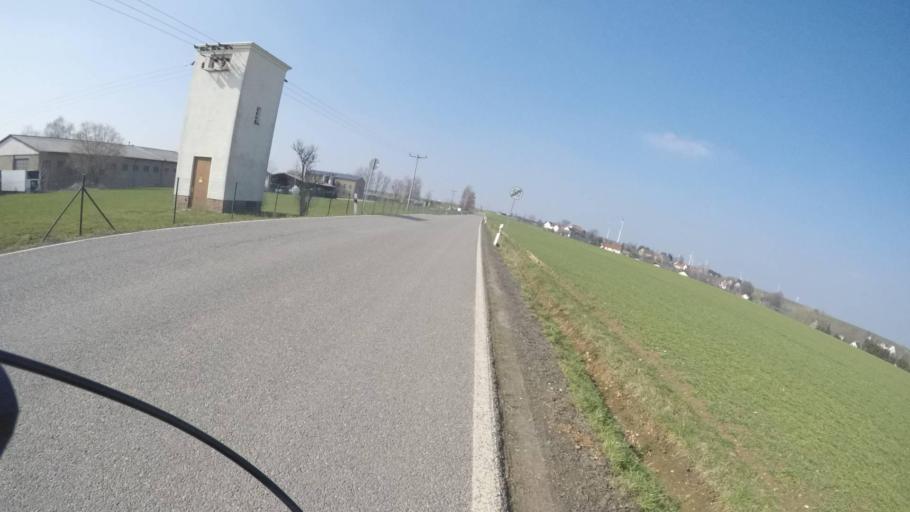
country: DE
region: Thuringia
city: Juckelberg
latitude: 50.9089
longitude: 12.6628
